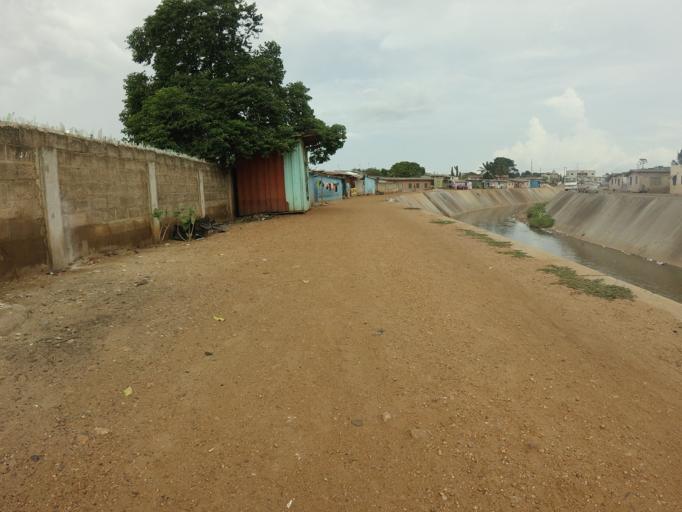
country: GH
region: Greater Accra
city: Accra
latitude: 5.5936
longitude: -0.2183
